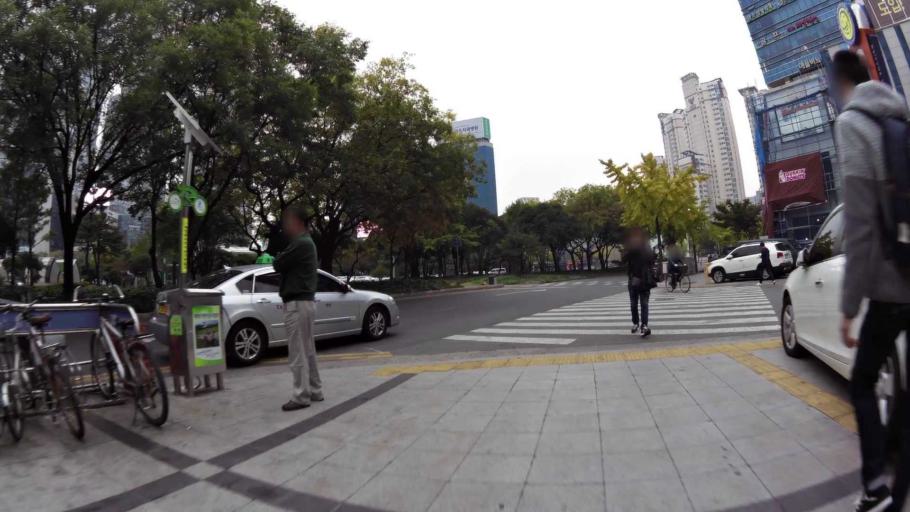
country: KR
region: Daegu
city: Daegu
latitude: 35.8587
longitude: 128.6251
